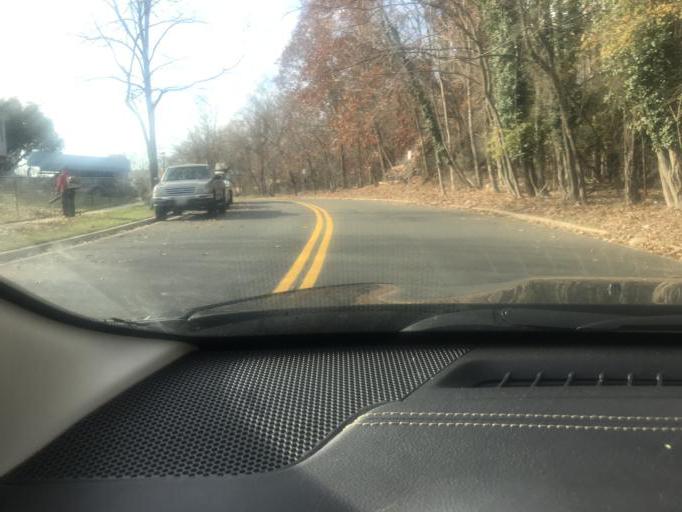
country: US
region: Maryland
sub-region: Prince George's County
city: Oxon Hill
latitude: 38.8152
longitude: -76.9818
